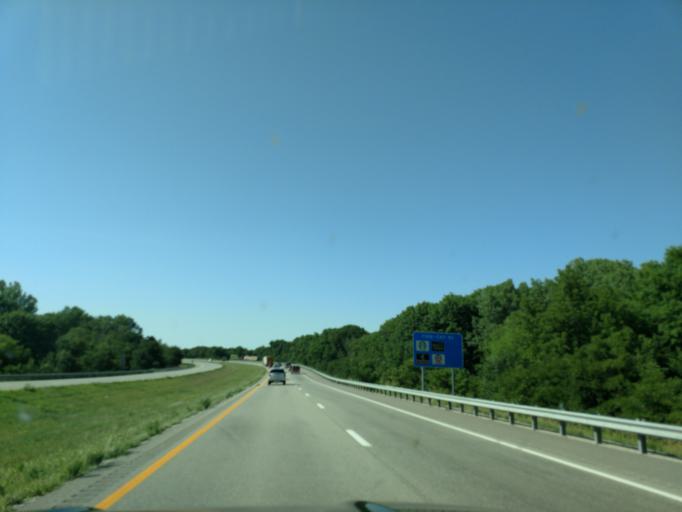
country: US
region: Missouri
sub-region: Andrew County
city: Country Club Village
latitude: 39.8495
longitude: -94.8052
